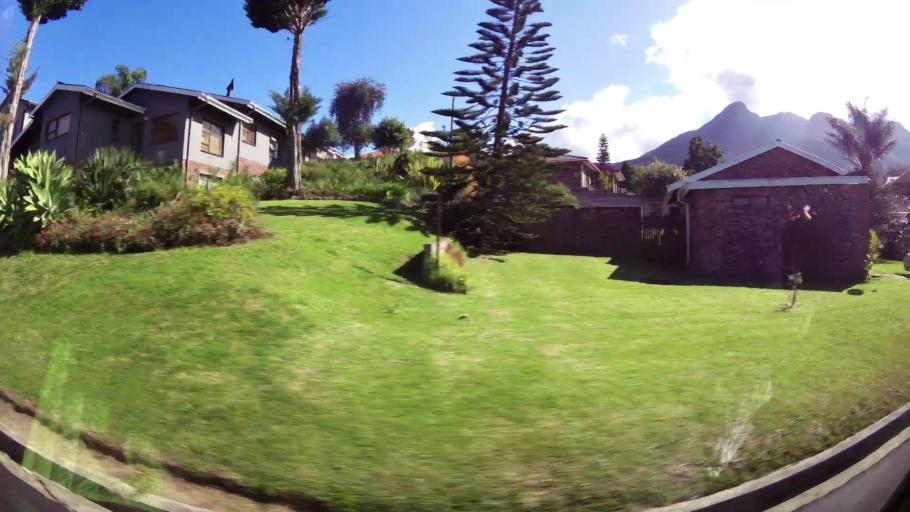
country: ZA
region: Western Cape
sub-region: Eden District Municipality
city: George
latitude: -33.9467
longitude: 22.4766
